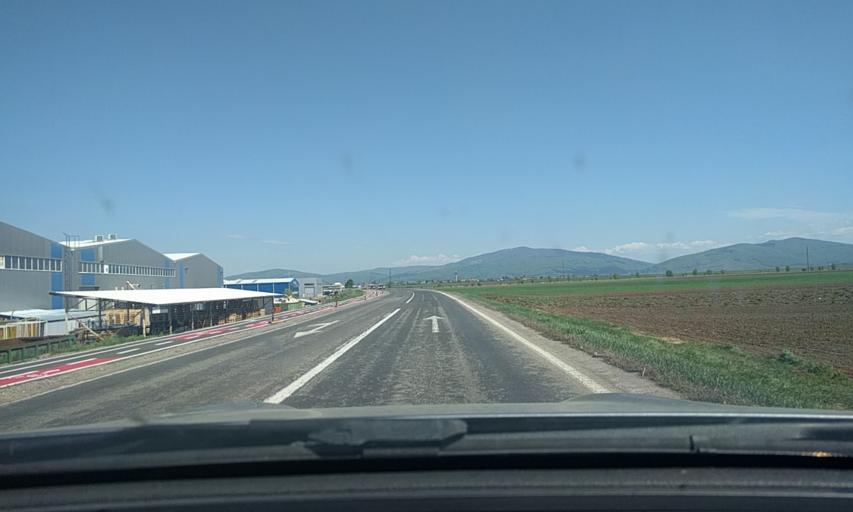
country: RO
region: Brasov
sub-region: Comuna Prejmer
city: Prejmer
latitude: 45.7146
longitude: 25.7391
